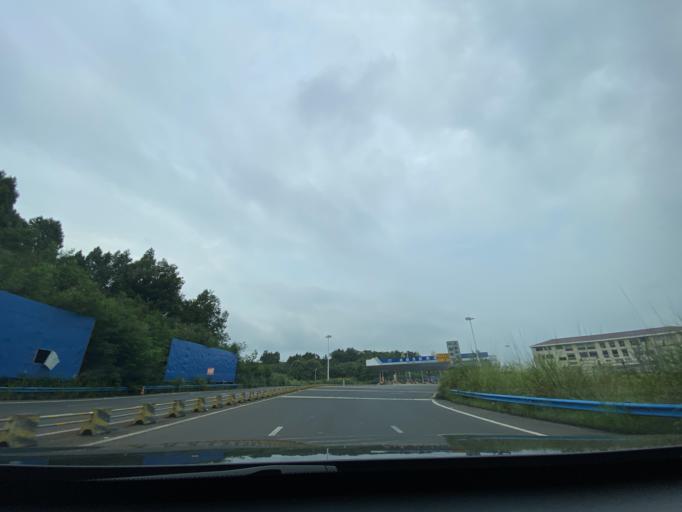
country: CN
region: Sichuan
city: Jiancheng
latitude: 30.5005
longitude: 104.4461
